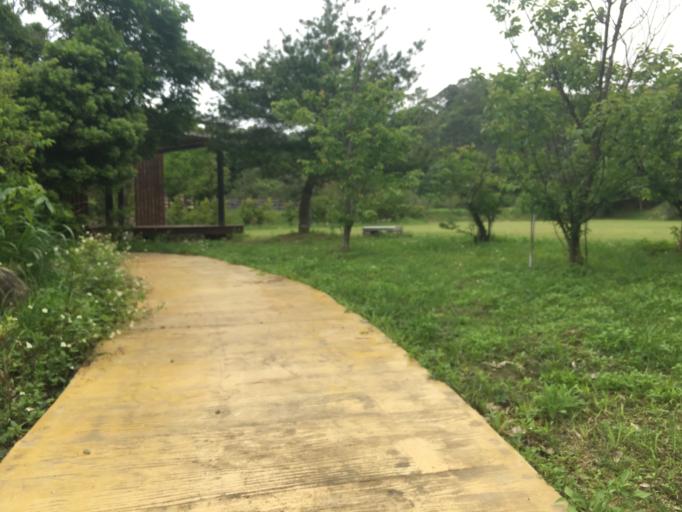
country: TW
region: Taiwan
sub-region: Hsinchu
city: Hsinchu
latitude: 24.7412
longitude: 120.9776
